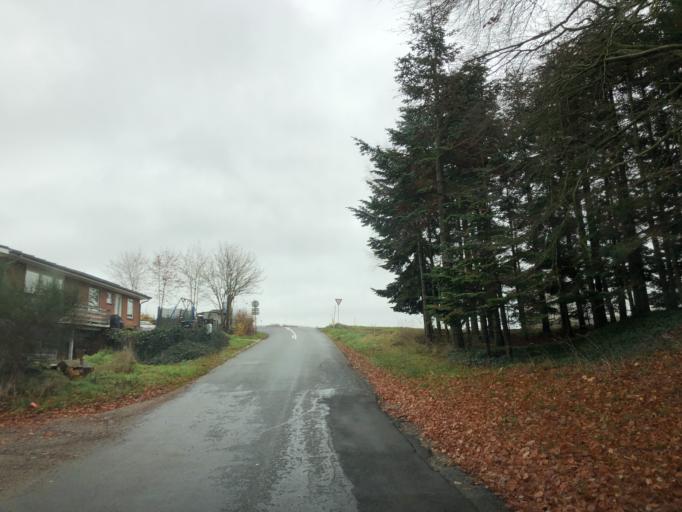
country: DK
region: Central Jutland
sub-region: Silkeborg Kommune
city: Svejbaek
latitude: 56.0979
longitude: 9.6077
